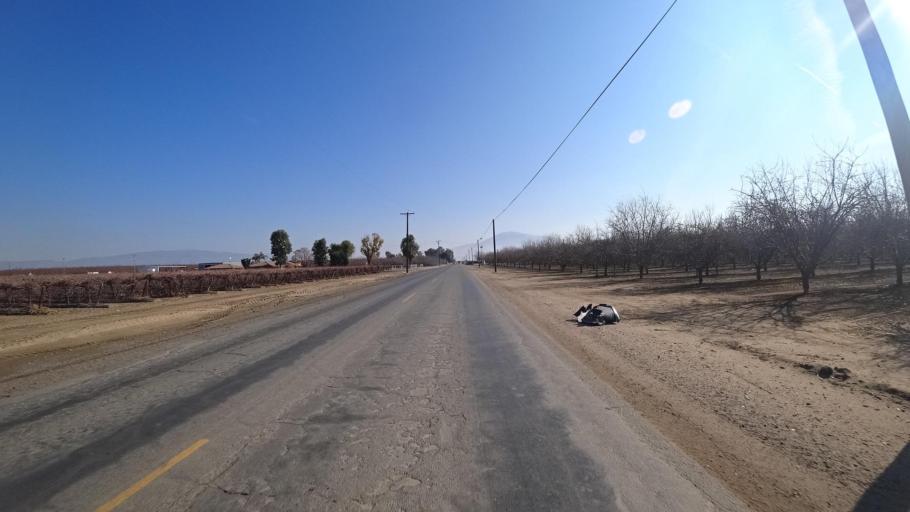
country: US
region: California
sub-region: Kern County
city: Weedpatch
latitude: 35.2379
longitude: -118.9027
